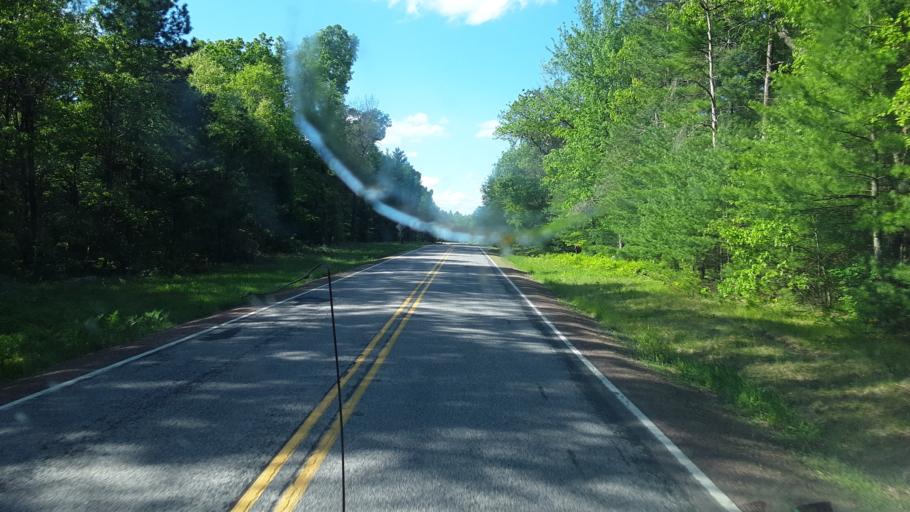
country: US
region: Wisconsin
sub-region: Wood County
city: Nekoosa
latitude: 44.3026
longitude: -90.1263
